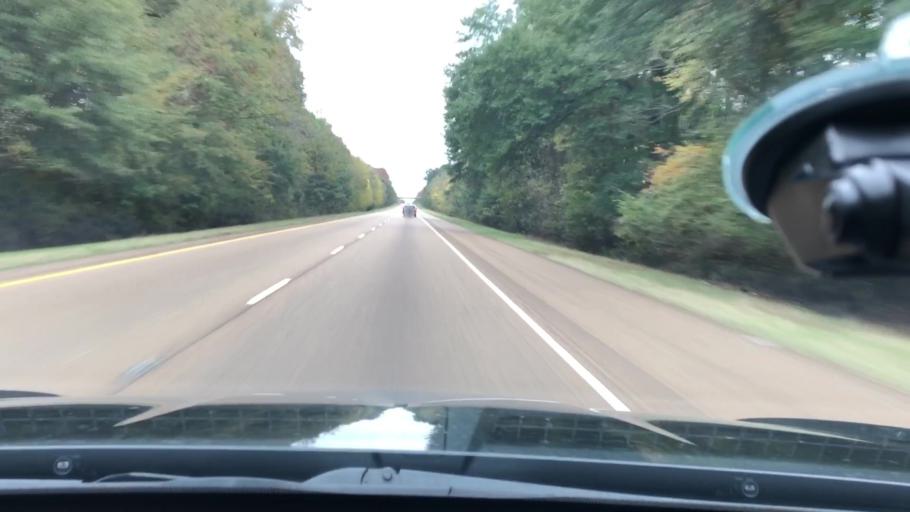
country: US
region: Arkansas
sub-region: Nevada County
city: Prescott
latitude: 33.7614
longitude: -93.4905
